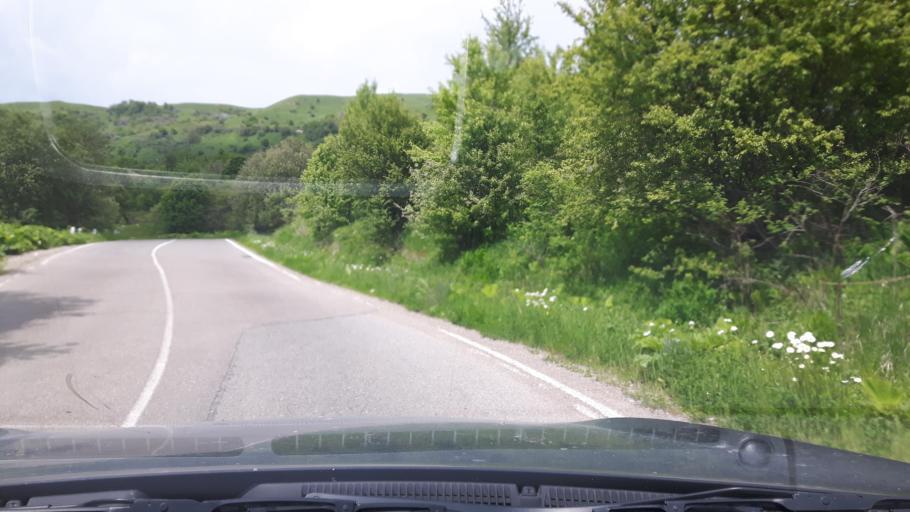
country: GE
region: Kakheti
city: Sagarejo
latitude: 41.8692
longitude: 45.2660
